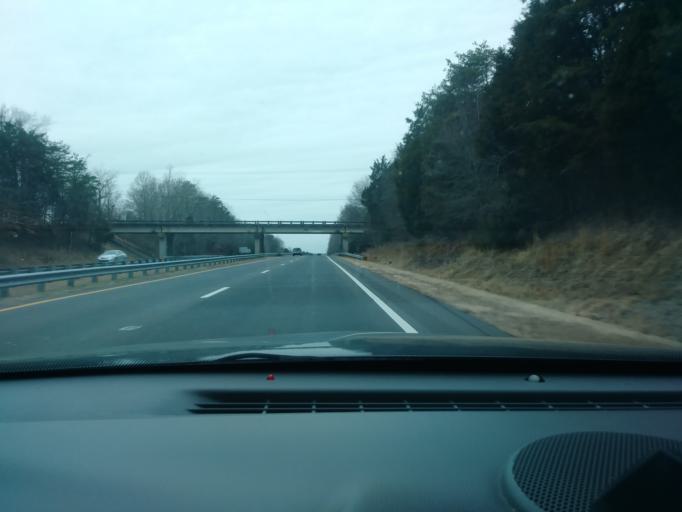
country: US
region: North Carolina
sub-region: Forsyth County
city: Lewisville
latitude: 36.1017
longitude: -80.4880
